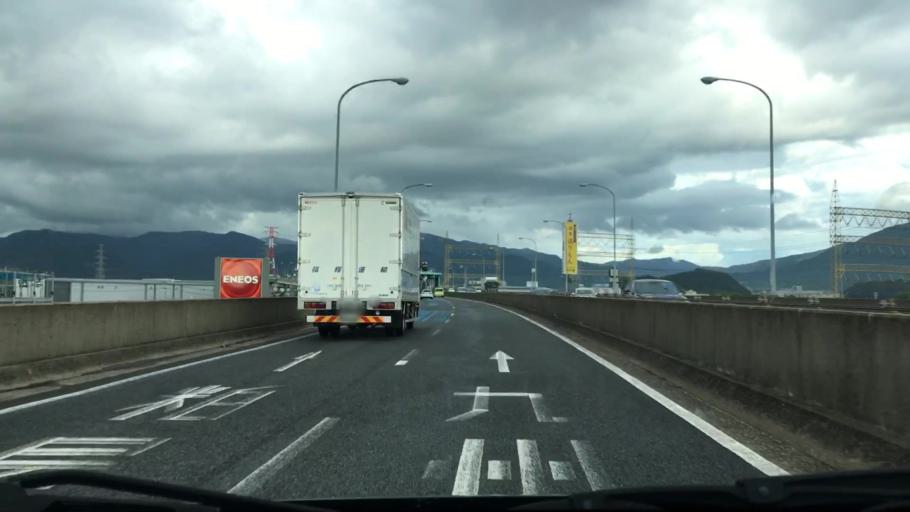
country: JP
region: Fukuoka
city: Fukuoka-shi
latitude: 33.6255
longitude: 130.4650
